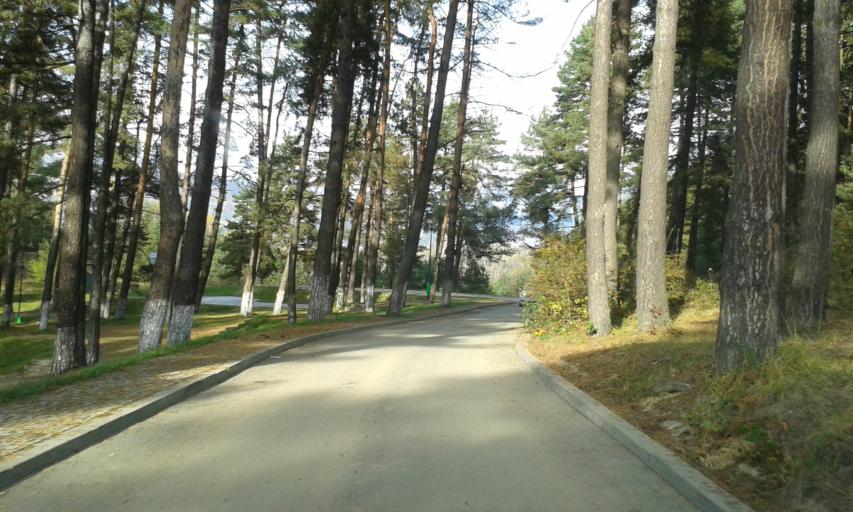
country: RO
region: Hunedoara
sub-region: Municipiul Petrosani
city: Petrosani
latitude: 45.4202
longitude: 23.3818
